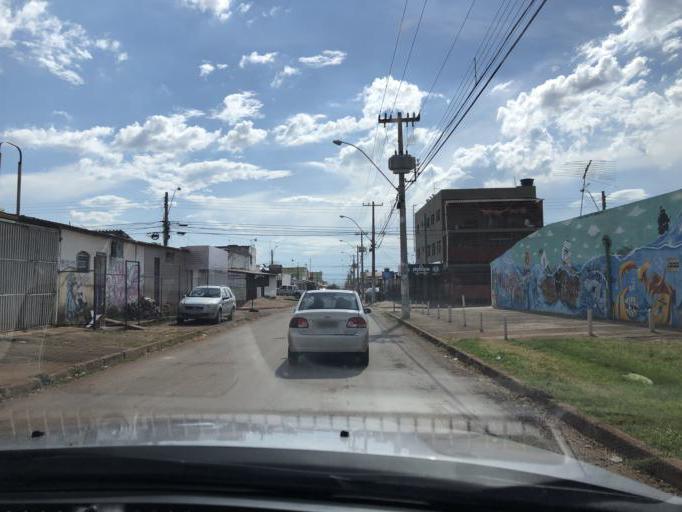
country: BR
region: Federal District
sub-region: Brasilia
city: Brasilia
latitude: -15.7942
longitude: -48.1227
